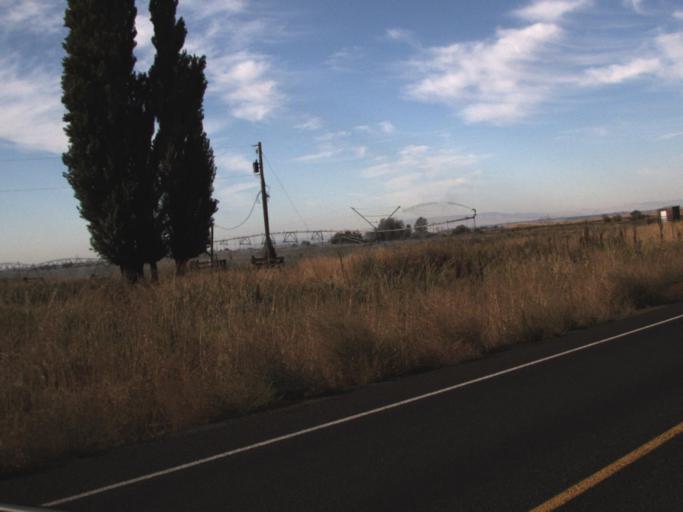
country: US
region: Washington
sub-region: Franklin County
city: Connell
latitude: 46.6637
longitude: -118.9771
